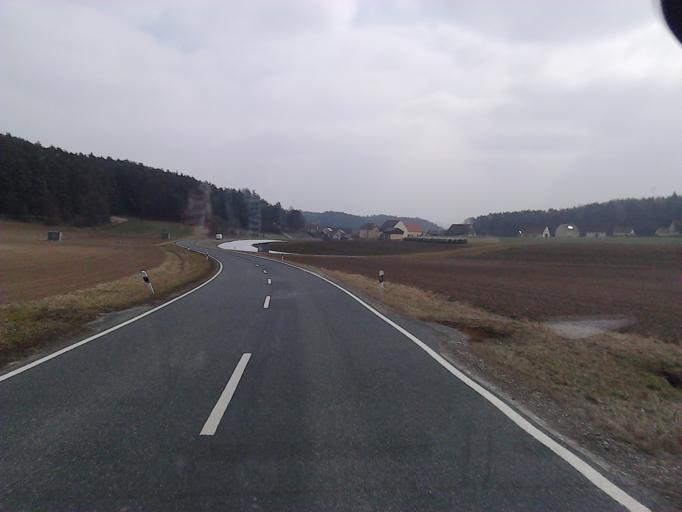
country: DE
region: Bavaria
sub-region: Regierungsbezirk Mittelfranken
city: Velden
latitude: 49.6444
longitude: 11.5013
